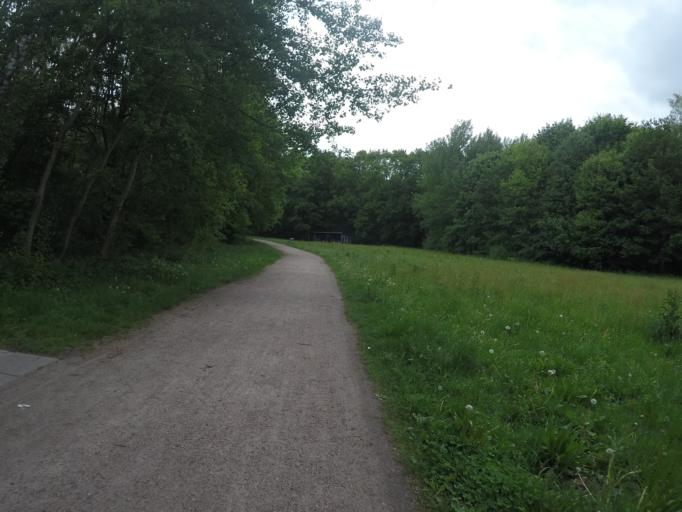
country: DE
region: Schleswig-Holstein
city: Bonningstedt
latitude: 53.6462
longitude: 9.9474
